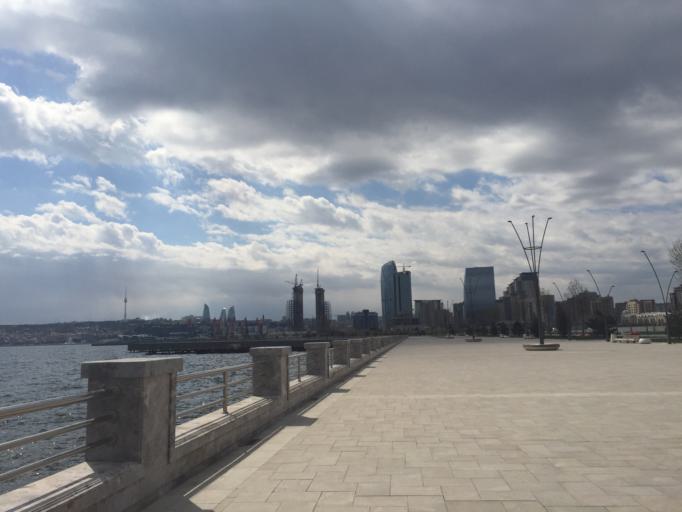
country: AZ
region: Baki
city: Baku
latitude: 40.3748
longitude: 49.8759
